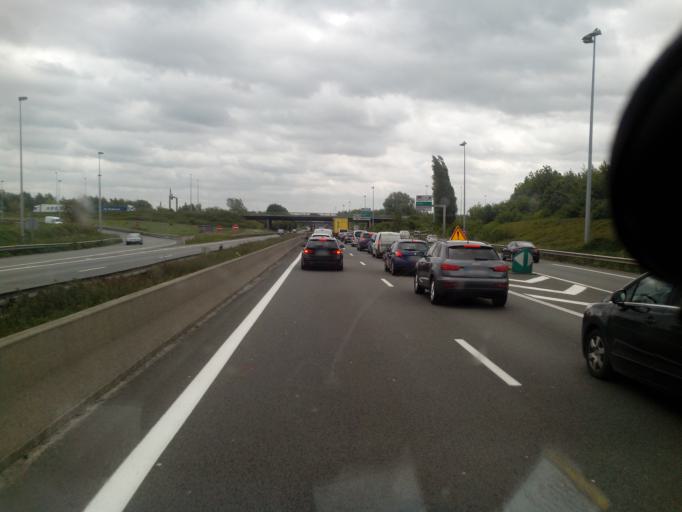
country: FR
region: Nord-Pas-de-Calais
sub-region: Departement du Nord
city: Capinghem
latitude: 50.6300
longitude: 2.9565
